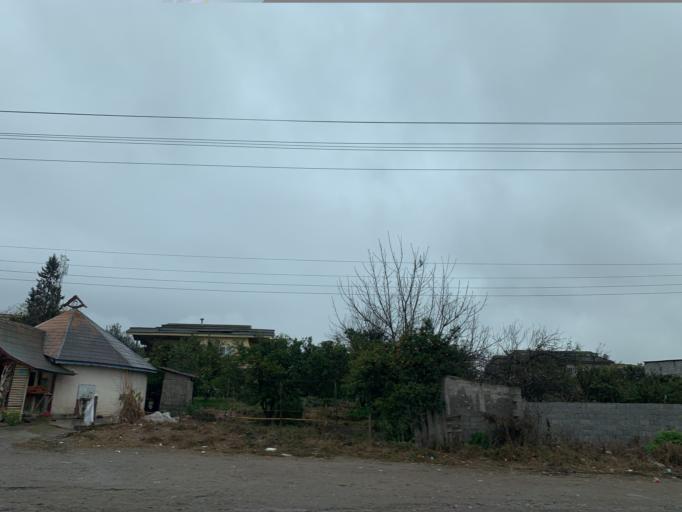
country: IR
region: Mazandaran
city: Amol
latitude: 36.4052
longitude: 52.3472
